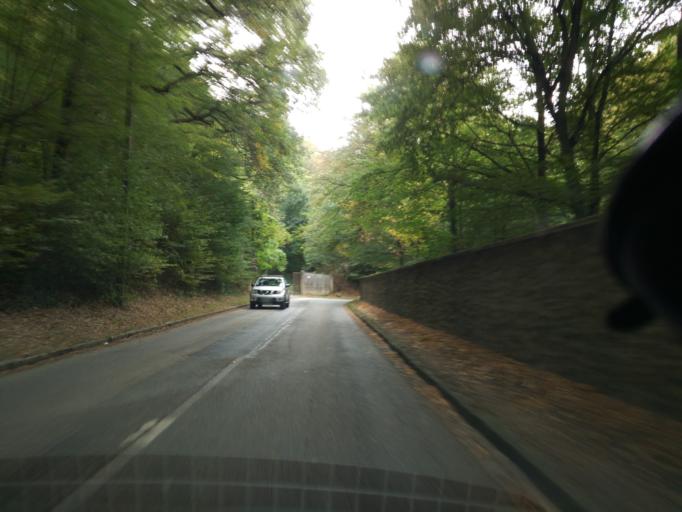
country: FR
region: Ile-de-France
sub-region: Departement des Yvelines
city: Saint-Remy-les-Chevreuse
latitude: 48.6926
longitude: 2.0675
